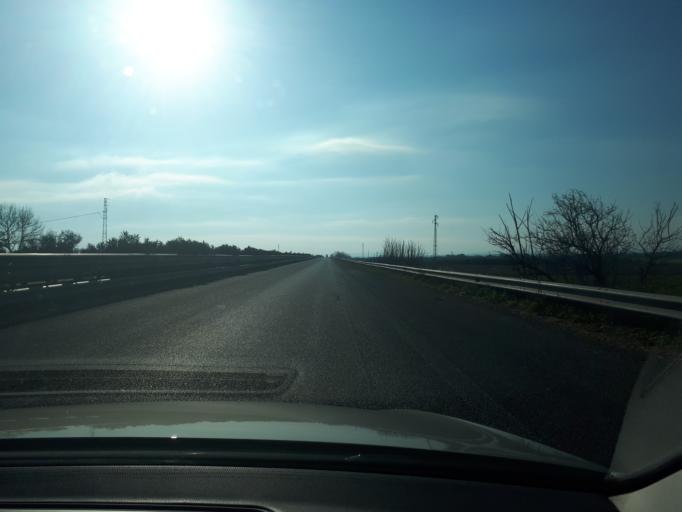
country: IT
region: Apulia
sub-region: Provincia di Foggia
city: Foggia
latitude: 41.4131
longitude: 15.5586
